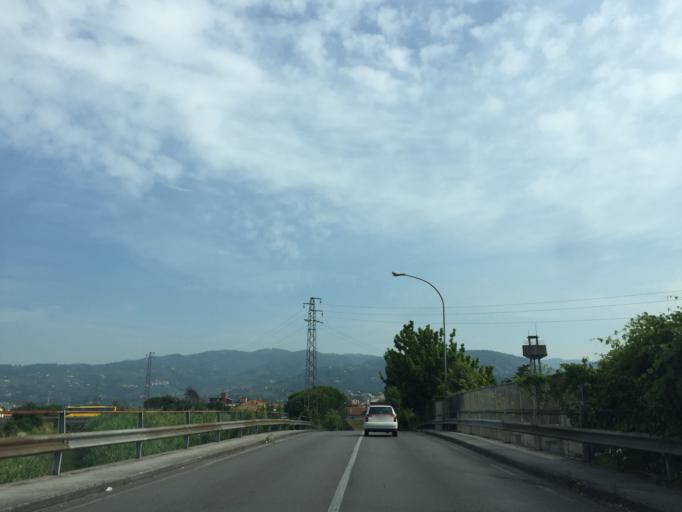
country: IT
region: Tuscany
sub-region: Provincia di Pistoia
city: Montecatini-Terme
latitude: 43.8698
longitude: 10.7679
